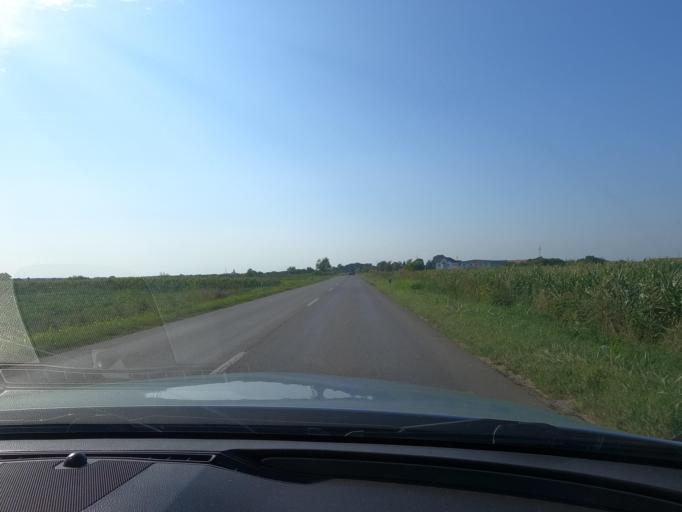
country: RS
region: Autonomna Pokrajina Vojvodina
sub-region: Juznobacki Okrug
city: Kovilj
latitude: 45.2880
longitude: 19.9666
